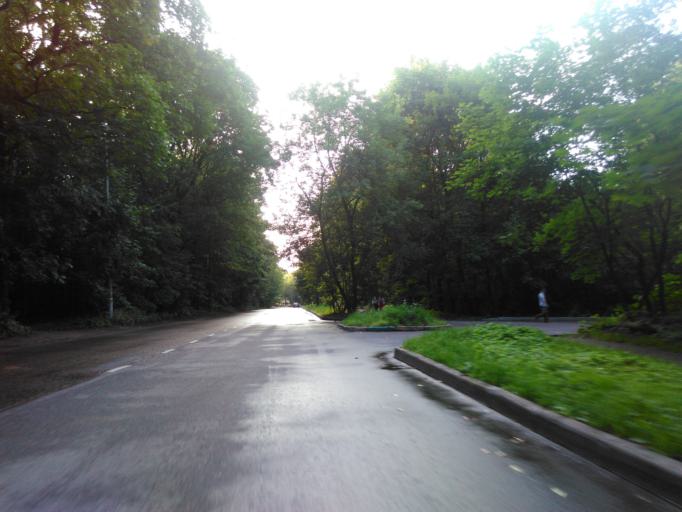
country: RU
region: Moscow
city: Sokol'niki
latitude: 55.8063
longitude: 37.6609
